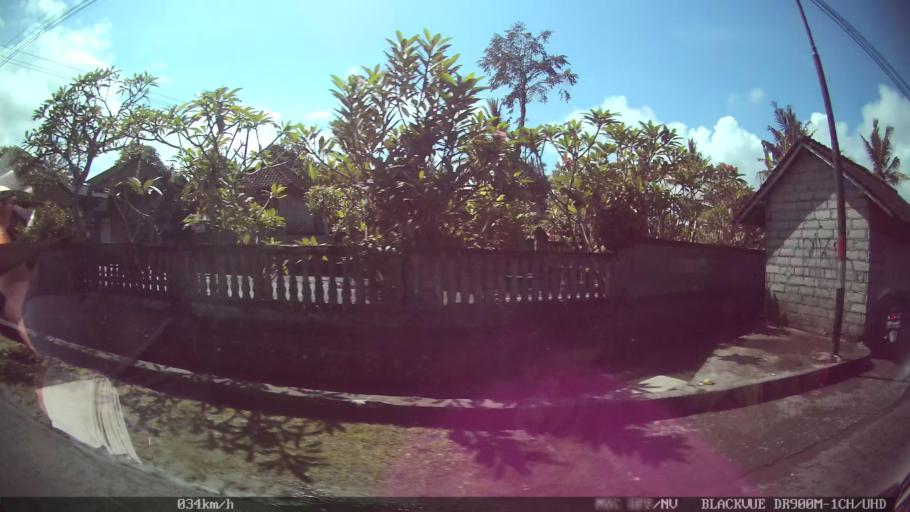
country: ID
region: Bali
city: Banjar Tebongkang
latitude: -8.5460
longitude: 115.2680
